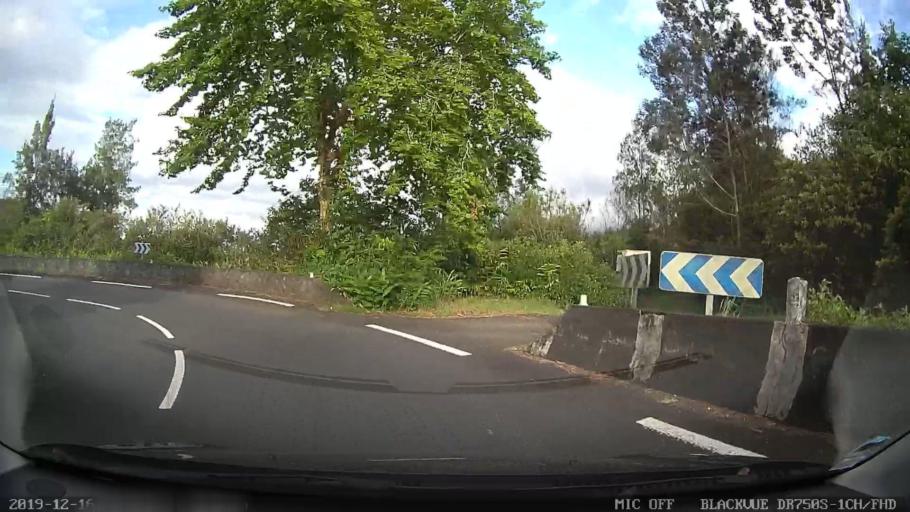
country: RE
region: Reunion
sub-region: Reunion
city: Cilaos
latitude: -21.1518
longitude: 55.6160
